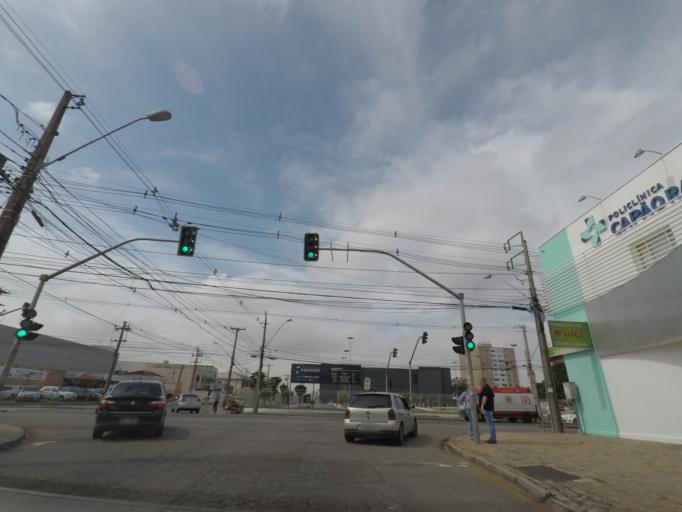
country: BR
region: Parana
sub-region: Curitiba
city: Curitiba
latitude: -25.4890
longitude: -49.2944
